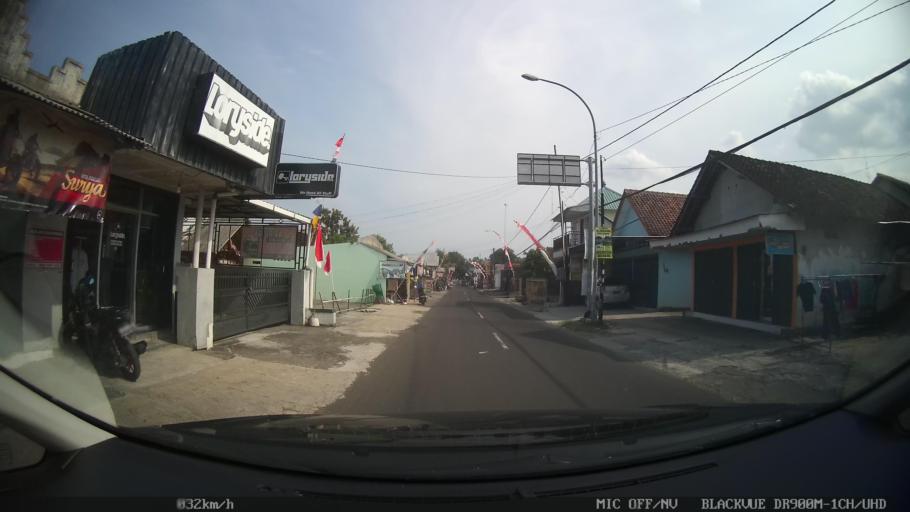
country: ID
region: Daerah Istimewa Yogyakarta
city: Depok
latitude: -7.7660
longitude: 110.4251
